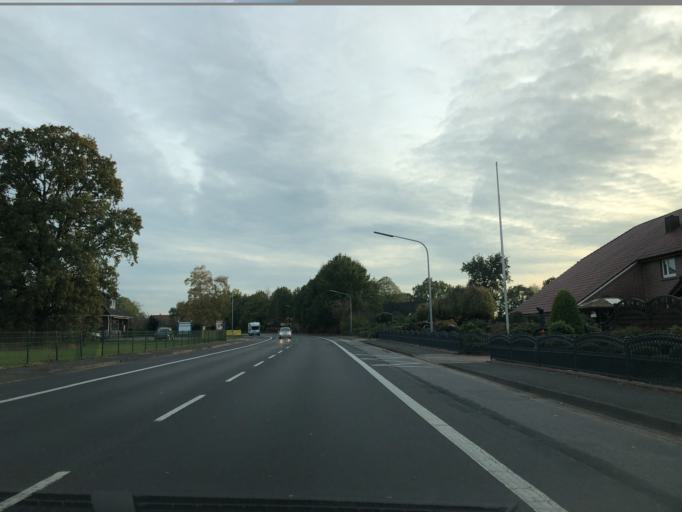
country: DE
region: Lower Saxony
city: Lehe
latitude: 53.0297
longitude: 7.3244
